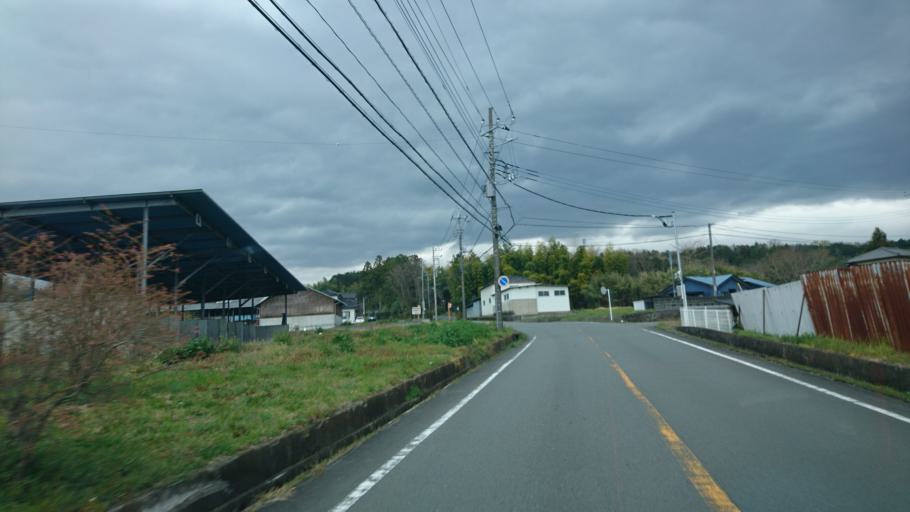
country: JP
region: Shizuoka
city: Fujinomiya
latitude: 35.2629
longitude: 138.6013
